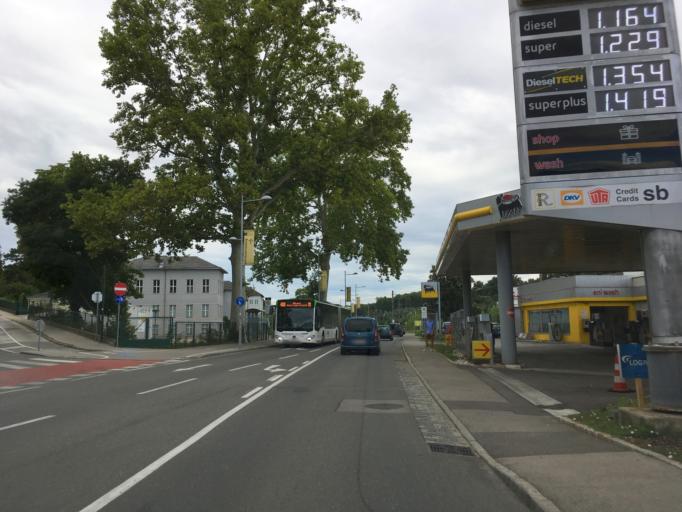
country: AT
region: Lower Austria
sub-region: Politischer Bezirk Wien-Umgebung
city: Klosterneuburg
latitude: 48.2999
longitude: 16.3327
